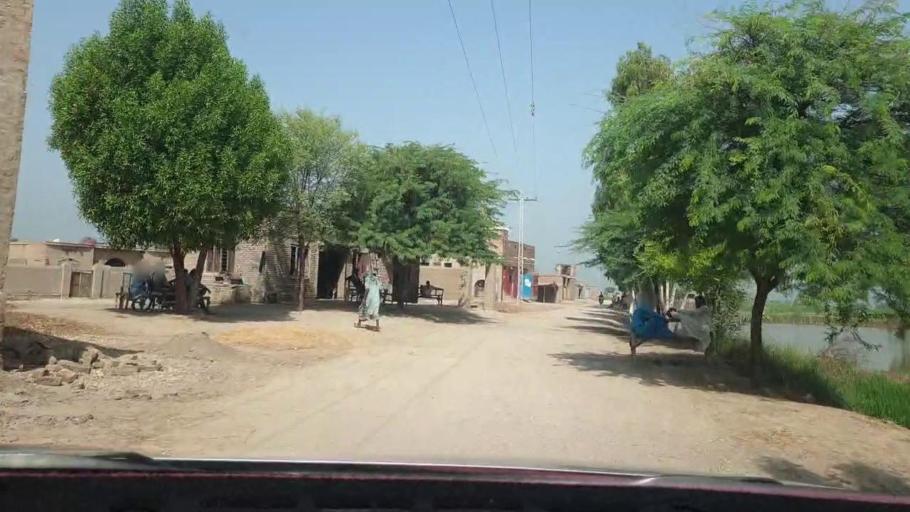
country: PK
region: Sindh
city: Nasirabad
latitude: 27.4226
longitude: 67.9113
